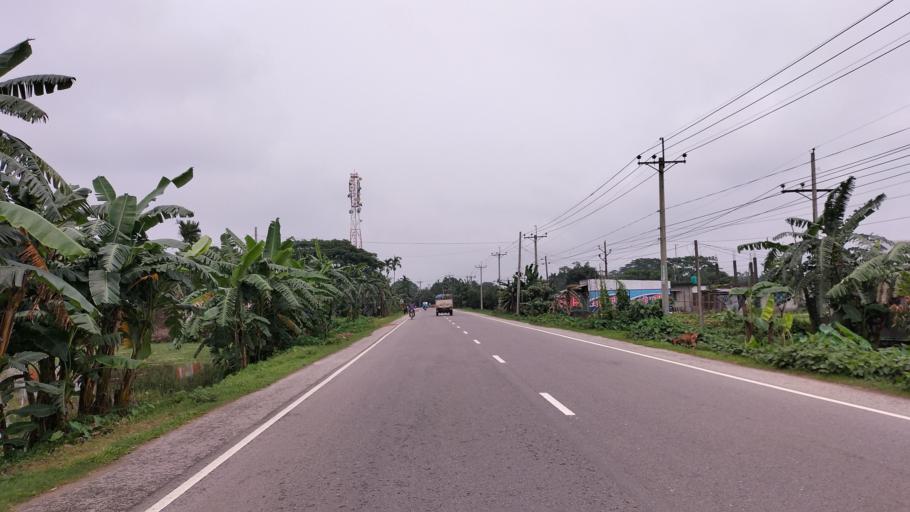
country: BD
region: Dhaka
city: Netrakona
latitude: 24.8496
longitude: 90.6415
